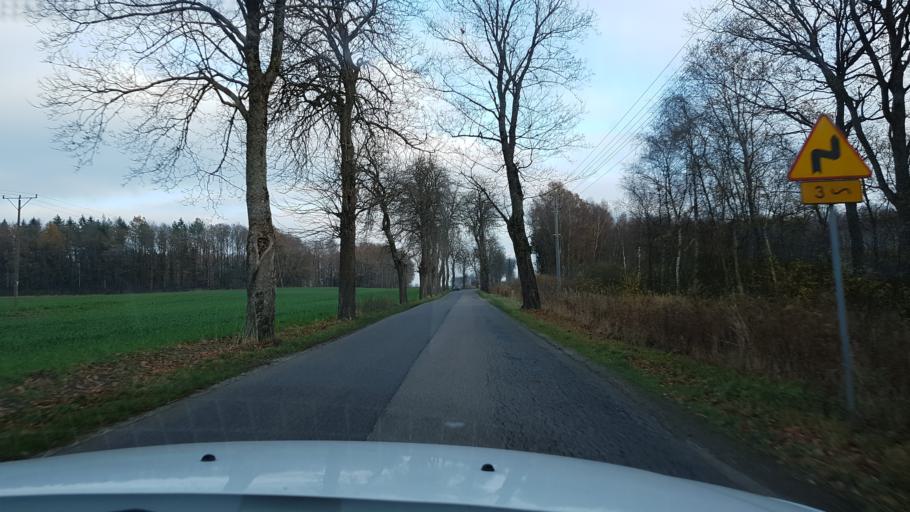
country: PL
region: West Pomeranian Voivodeship
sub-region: Powiat kolobrzeski
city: Goscino
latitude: 54.0526
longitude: 15.7134
